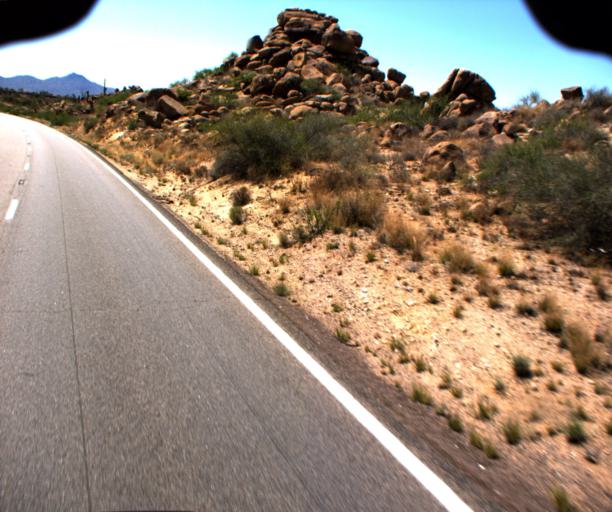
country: US
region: Arizona
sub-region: Yavapai County
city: Bagdad
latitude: 34.4849
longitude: -113.3617
